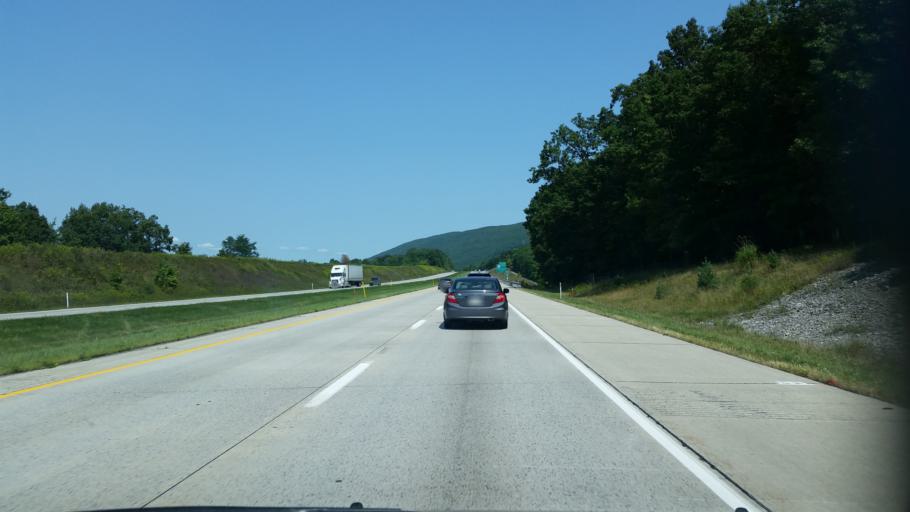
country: US
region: Pennsylvania
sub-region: Blair County
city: Greenwood
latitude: 40.5419
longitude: -78.3439
